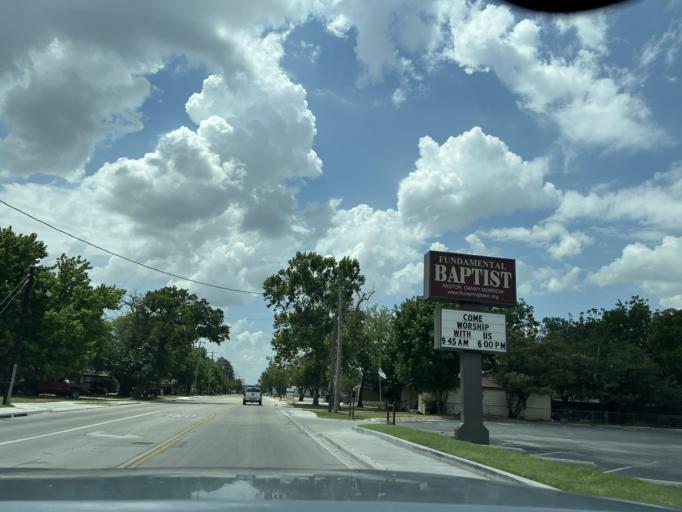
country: US
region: Texas
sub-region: Parker County
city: Springtown
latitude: 32.9707
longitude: -97.6849
